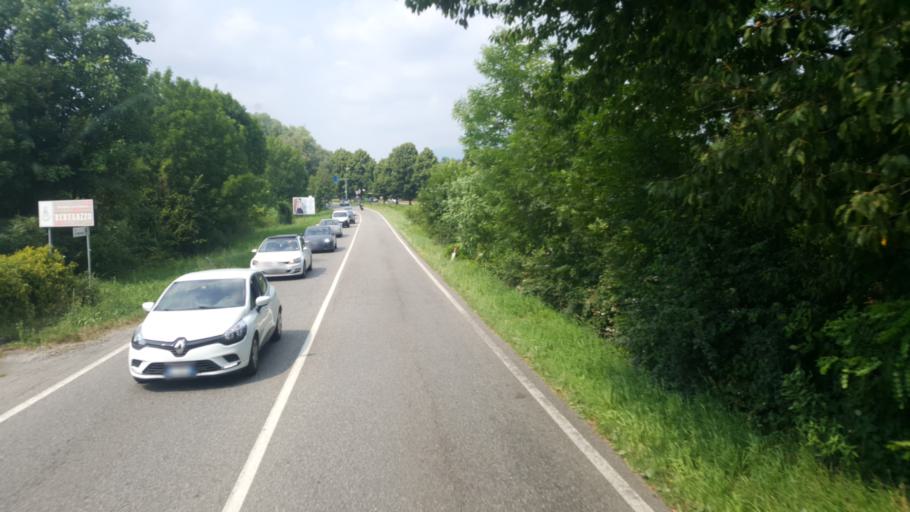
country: IT
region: Lombardy
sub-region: Provincia di Como
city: Beregazzo
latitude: 45.7733
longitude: 8.9615
